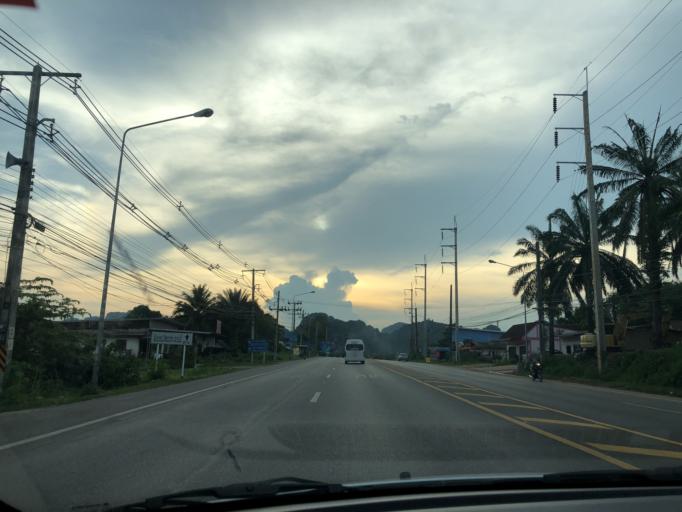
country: TH
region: Krabi
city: Krabi
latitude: 8.0833
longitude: 98.8898
